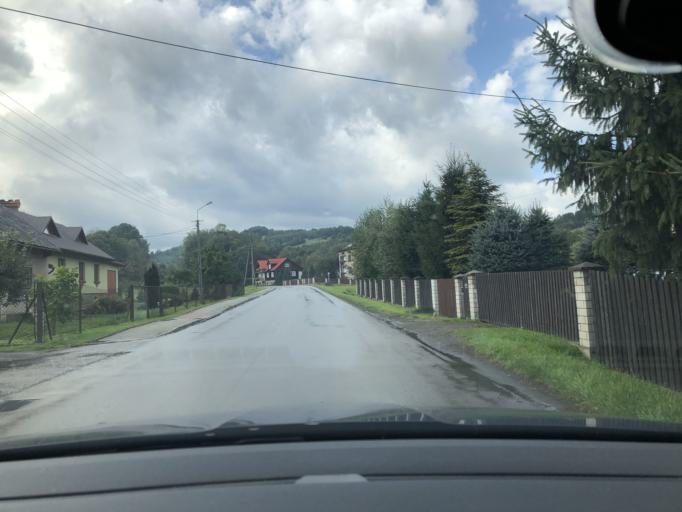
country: PL
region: Lesser Poland Voivodeship
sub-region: Powiat suski
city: Lachowice
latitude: 49.7167
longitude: 19.4816
